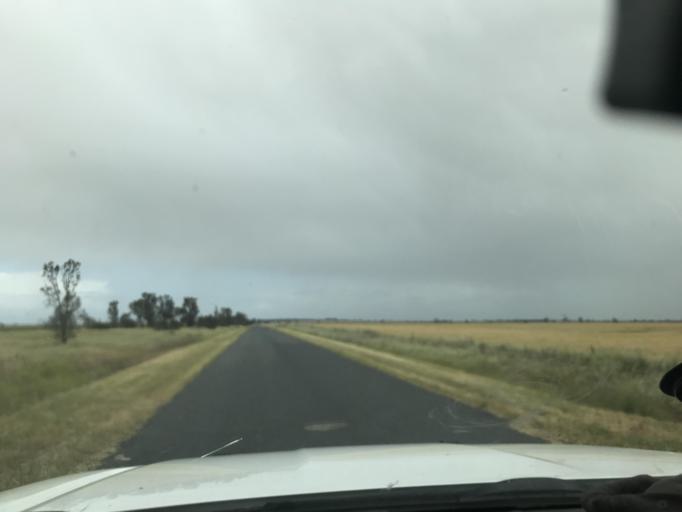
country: AU
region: South Australia
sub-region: Tatiara
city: Bordertown
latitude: -36.4125
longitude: 141.1821
